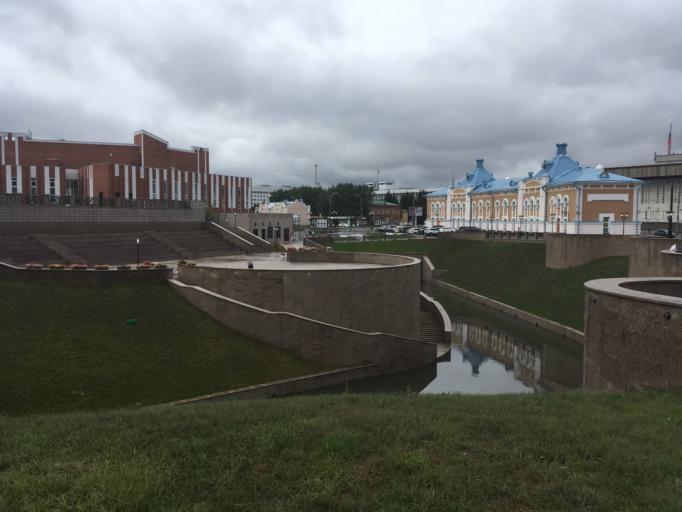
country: RU
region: Tomsk
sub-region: Tomskiy Rayon
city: Tomsk
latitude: 56.4881
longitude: 84.9506
